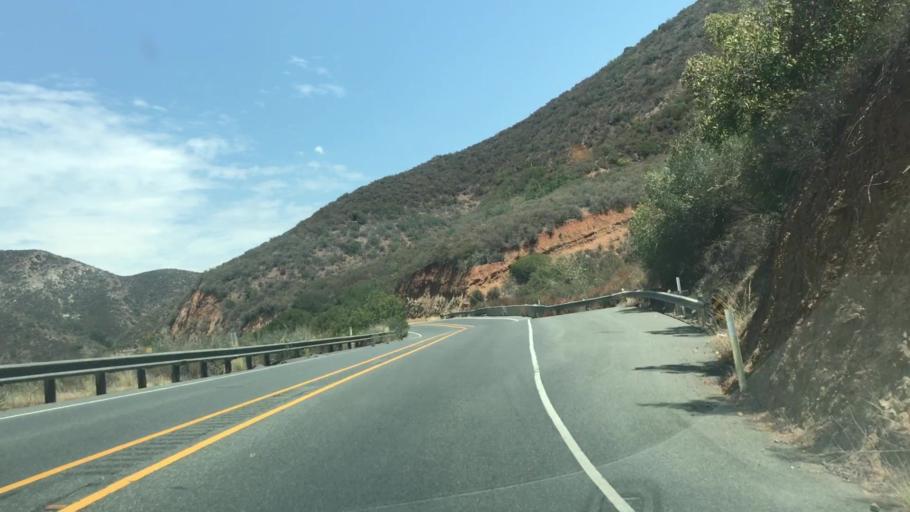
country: US
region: California
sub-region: Orange County
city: Coto De Caza
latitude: 33.5935
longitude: -117.4904
